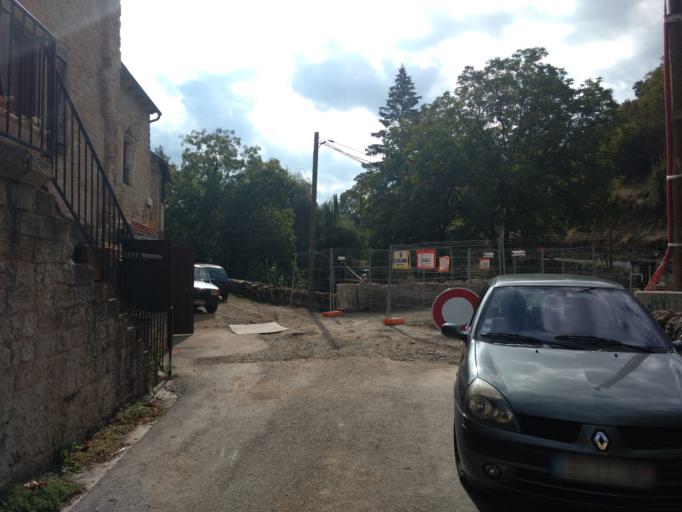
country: FR
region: Midi-Pyrenees
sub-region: Departement de l'Aveyron
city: Bozouls
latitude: 44.4681
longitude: 2.7167
